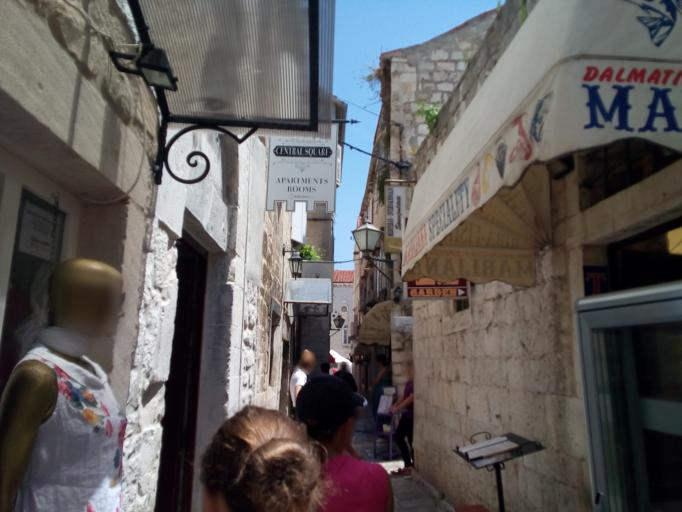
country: HR
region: Splitsko-Dalmatinska
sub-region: Grad Trogir
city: Trogir
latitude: 43.5169
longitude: 16.2506
